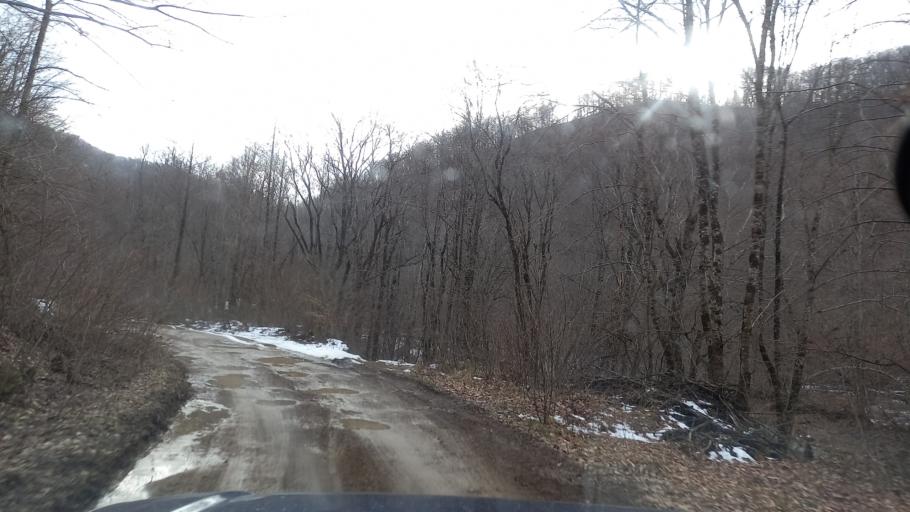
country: RU
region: Adygeya
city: Kamennomostskiy
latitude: 44.1606
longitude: 40.2980
